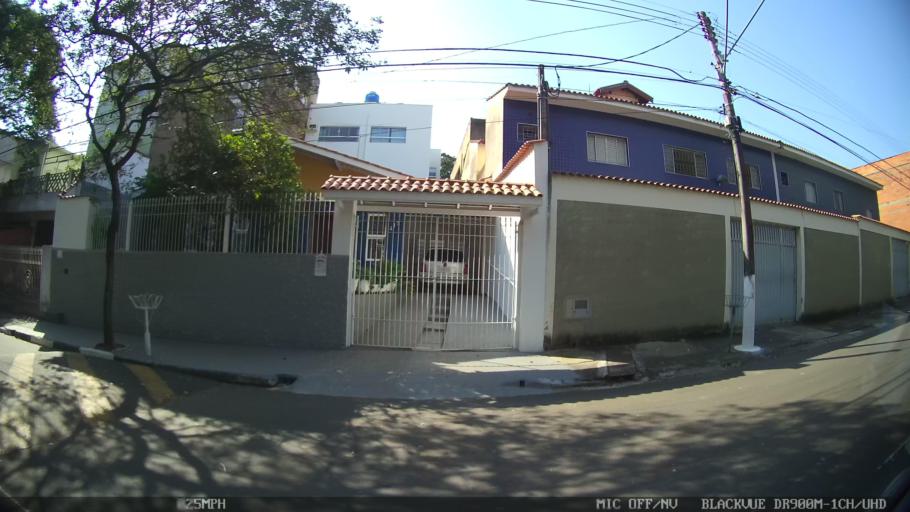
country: BR
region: Sao Paulo
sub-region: Paulinia
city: Paulinia
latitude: -22.7633
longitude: -47.1541
